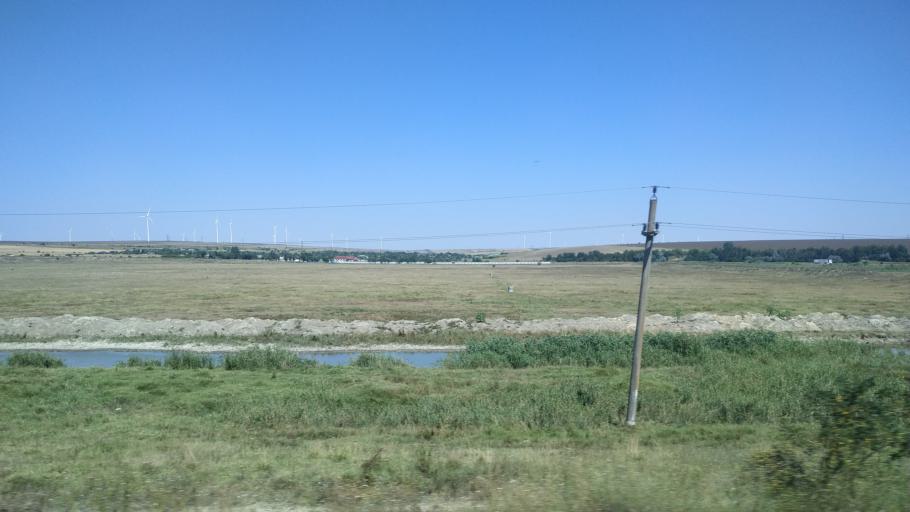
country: RO
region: Constanta
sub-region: Comuna Mircea Voda
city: Mircea Voda
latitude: 44.2637
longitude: 28.1729
